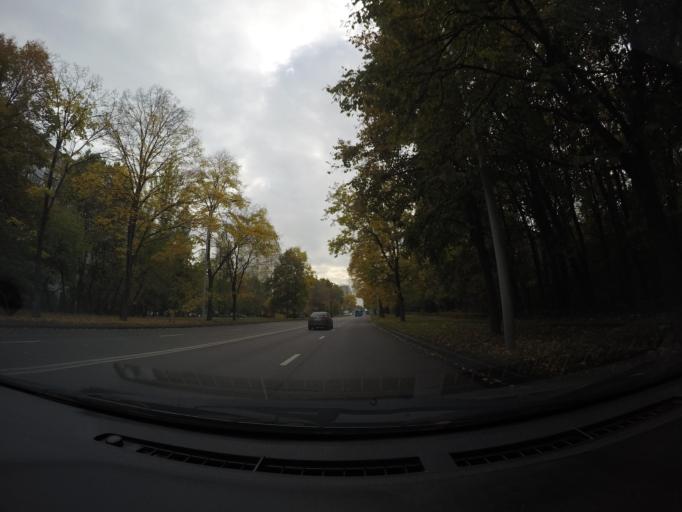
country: RU
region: Moskovskaya
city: Novogireyevo
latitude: 55.7637
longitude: 37.8222
